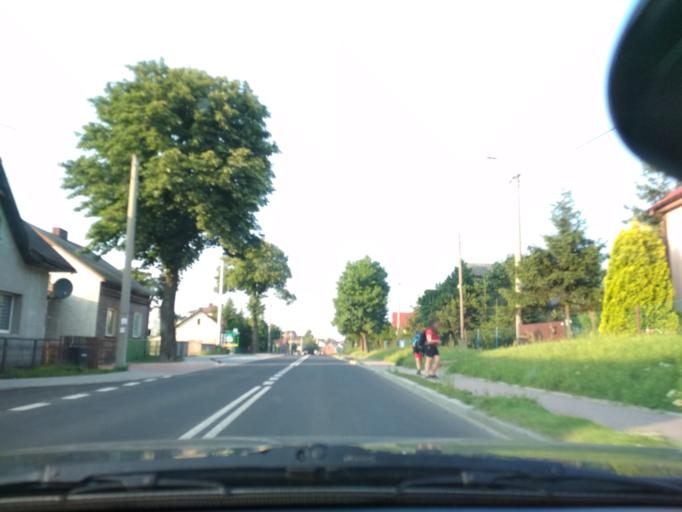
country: PL
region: Silesian Voivodeship
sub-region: Powiat zawiercianski
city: Ogrodzieniec
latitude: 50.4550
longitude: 19.5491
